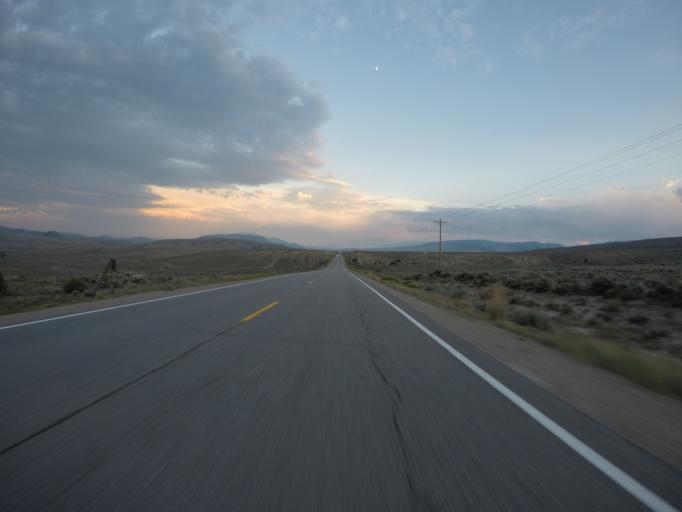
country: US
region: Colorado
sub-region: Grand County
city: Kremmling
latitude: 40.0987
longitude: -106.4218
